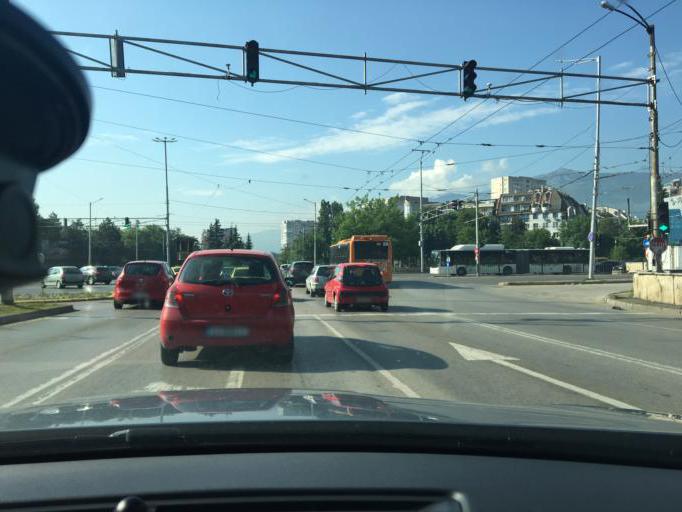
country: BG
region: Sofia-Capital
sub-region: Stolichna Obshtina
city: Sofia
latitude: 42.6798
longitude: 23.3022
